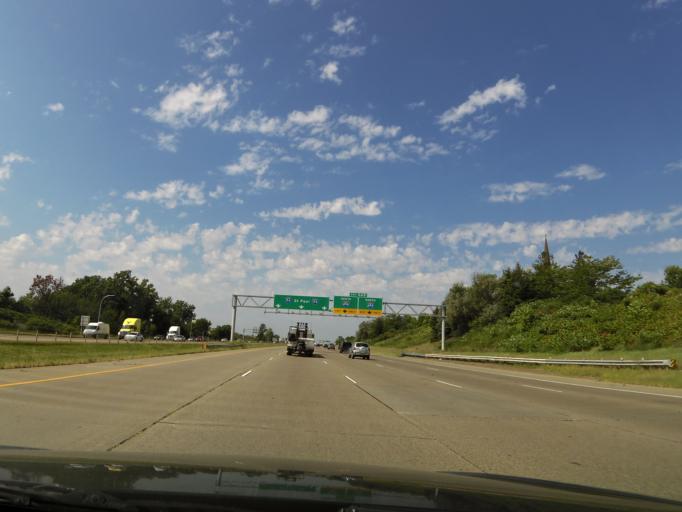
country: US
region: Minnesota
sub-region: Washington County
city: Oakdale
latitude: 44.9487
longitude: -92.9378
